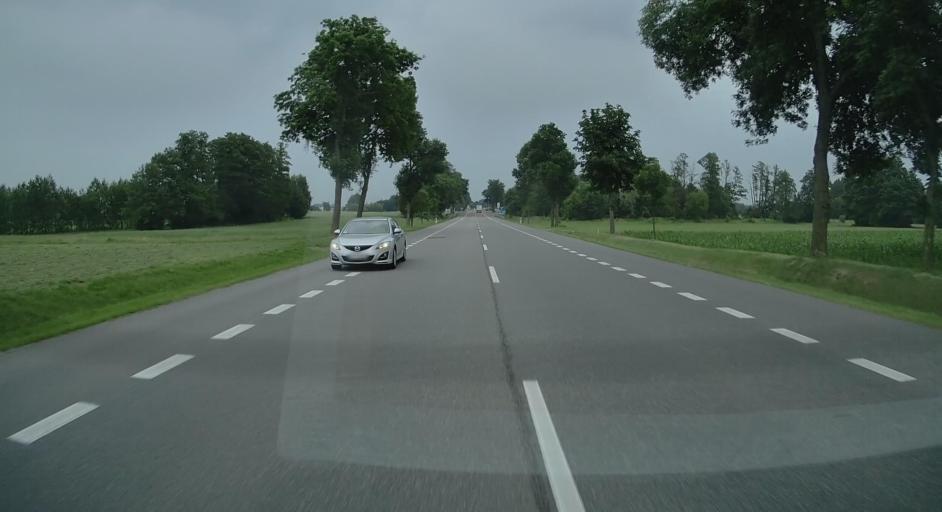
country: PL
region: Lublin Voivodeship
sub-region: Powiat lukowski
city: Trzebieszow
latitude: 52.0517
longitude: 22.6606
